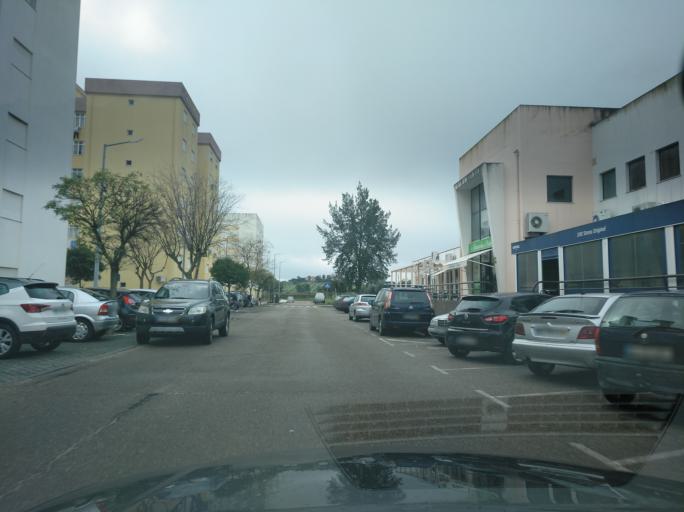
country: PT
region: Portalegre
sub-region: Elvas
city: Elvas
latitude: 38.8677
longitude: -7.1716
